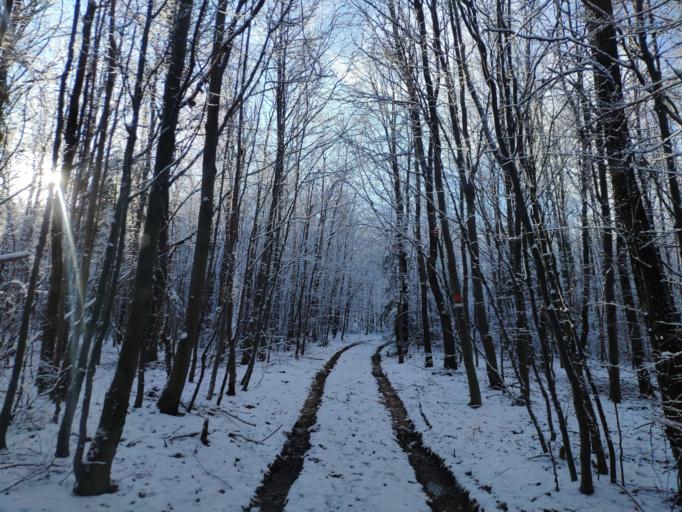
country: SK
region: Kosicky
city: Moldava nad Bodvou
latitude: 48.7402
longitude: 21.0974
